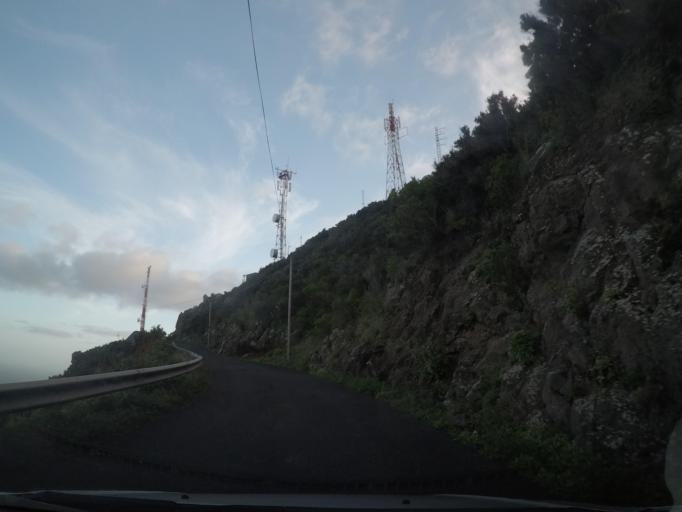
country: PT
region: Madeira
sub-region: Machico
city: Canical
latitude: 32.7248
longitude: -16.7591
